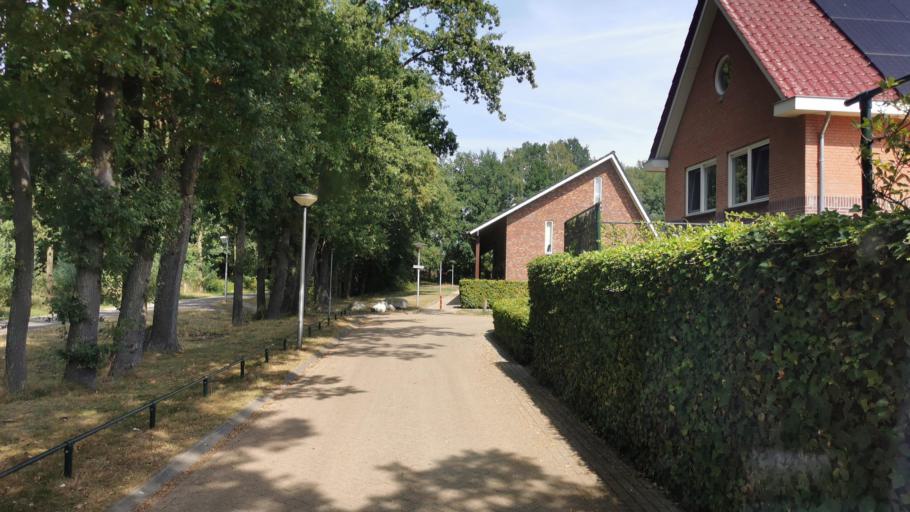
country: NL
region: Overijssel
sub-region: Gemeente Enschede
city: Enschede
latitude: 52.2128
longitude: 6.9566
